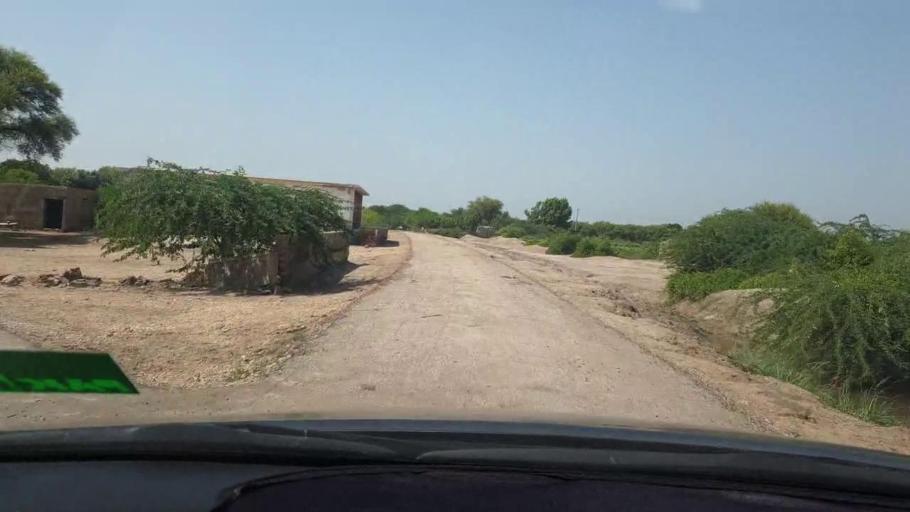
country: PK
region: Sindh
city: Digri
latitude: 24.9406
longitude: 69.1565
